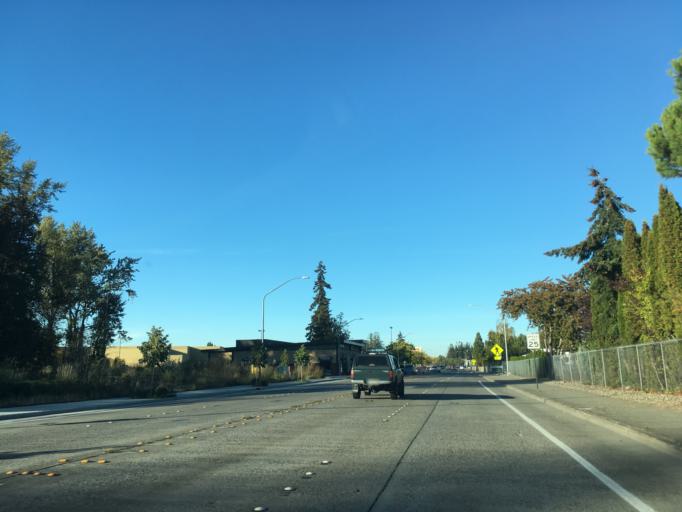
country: US
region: Washington
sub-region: Whatcom County
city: Bellingham
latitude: 48.7407
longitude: -122.4639
